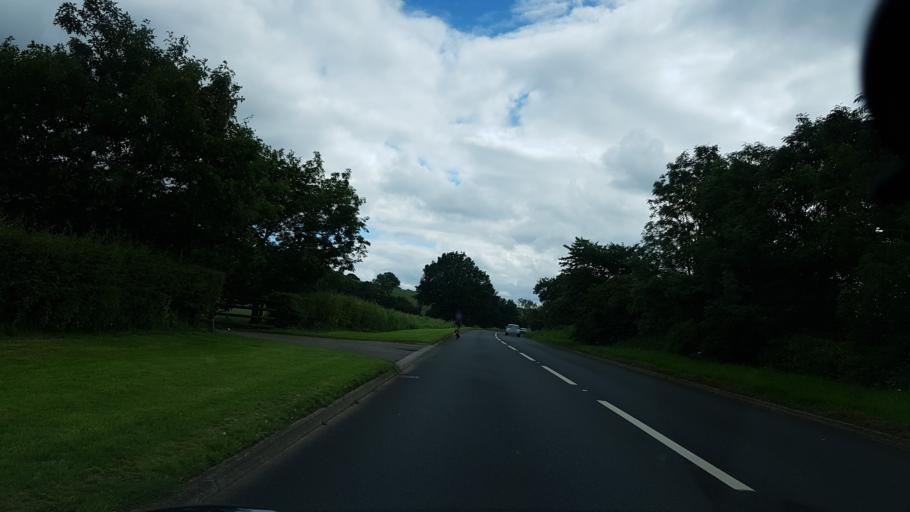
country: GB
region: Wales
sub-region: Monmouthshire
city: Abergavenny
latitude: 51.8697
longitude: -2.9897
